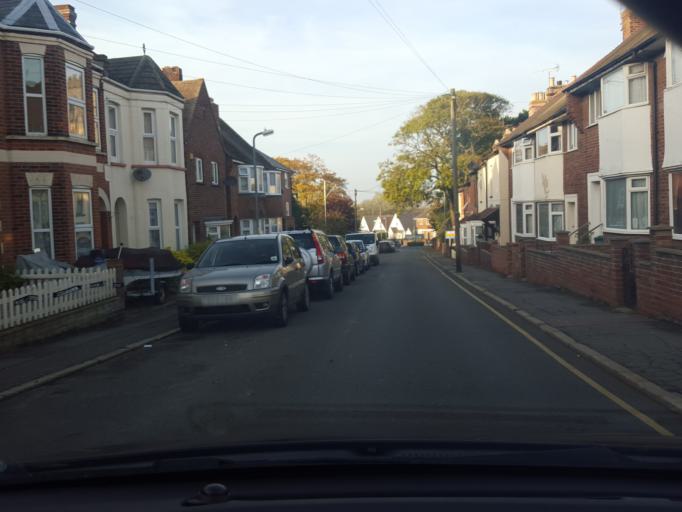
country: GB
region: England
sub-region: Essex
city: Walton-on-the-Naze
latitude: 51.8472
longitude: 1.2681
